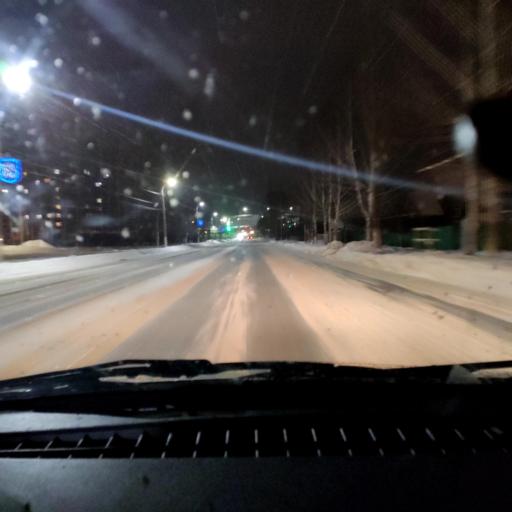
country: RU
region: Bashkortostan
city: Blagoveshchensk
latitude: 55.0527
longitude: 55.9515
